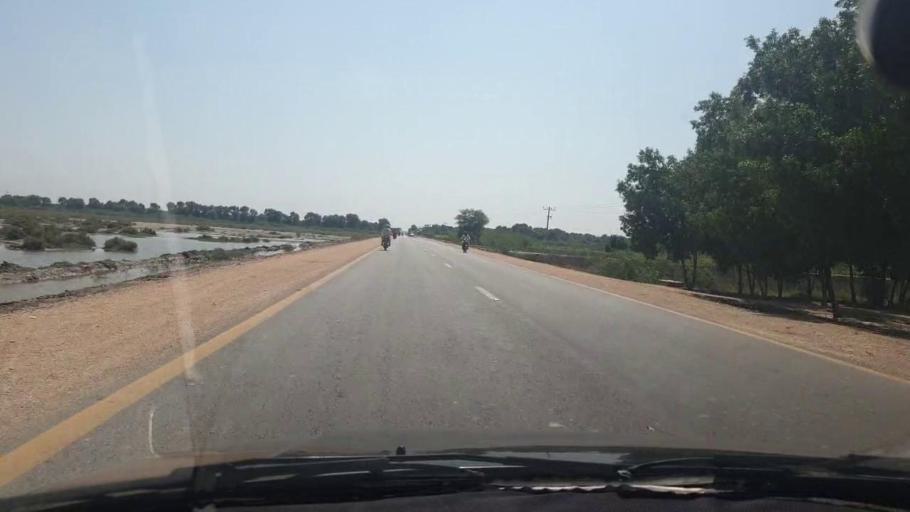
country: PK
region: Sindh
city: Chambar
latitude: 25.3274
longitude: 68.7996
